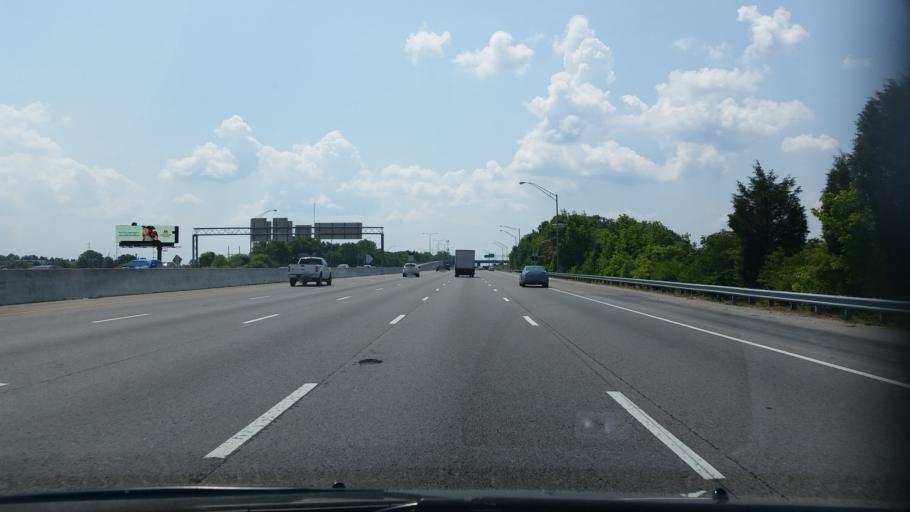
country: US
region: Tennessee
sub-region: Davidson County
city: Oak Hill
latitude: 36.1078
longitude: -86.7691
